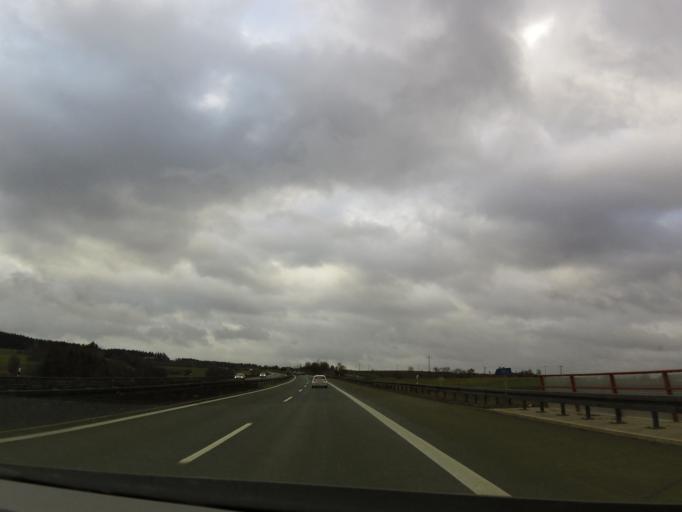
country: DE
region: Bavaria
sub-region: Upper Franconia
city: Regnitzlosau
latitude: 50.2897
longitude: 12.0228
